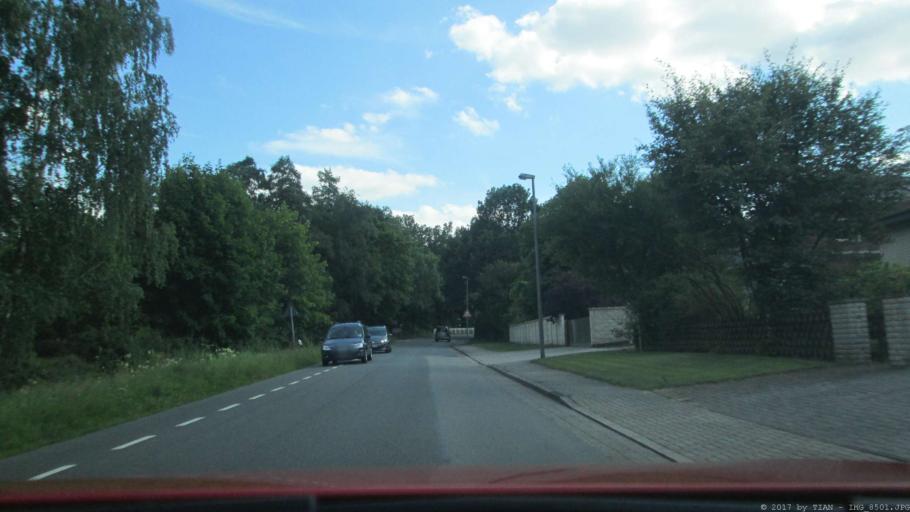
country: DE
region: Lower Saxony
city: Wolfsburg
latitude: 52.3795
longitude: 10.8006
